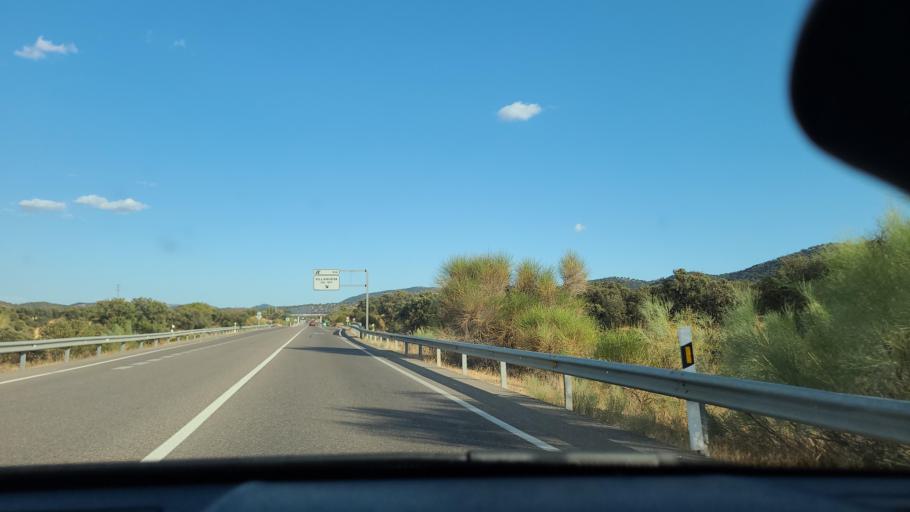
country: ES
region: Andalusia
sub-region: Province of Cordoba
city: Belmez
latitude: 38.2162
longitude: -5.1449
